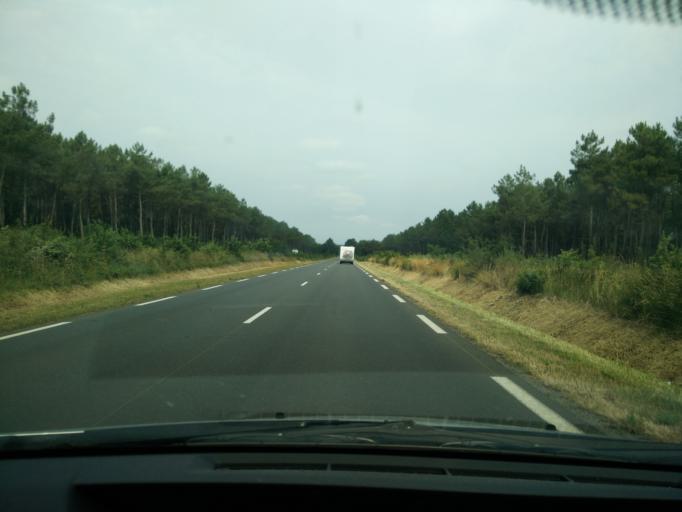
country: FR
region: Pays de la Loire
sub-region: Departement de Maine-et-Loire
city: Montreuil-Bellay
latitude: 47.1498
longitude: -0.1753
